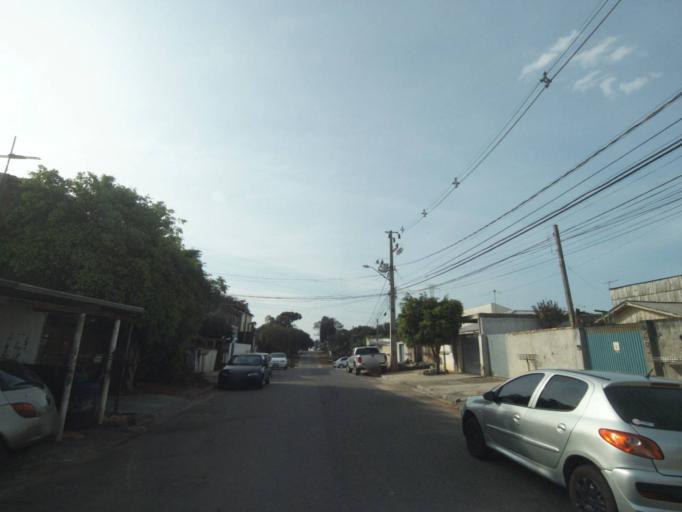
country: BR
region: Parana
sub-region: Curitiba
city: Curitiba
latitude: -25.4653
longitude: -49.3136
